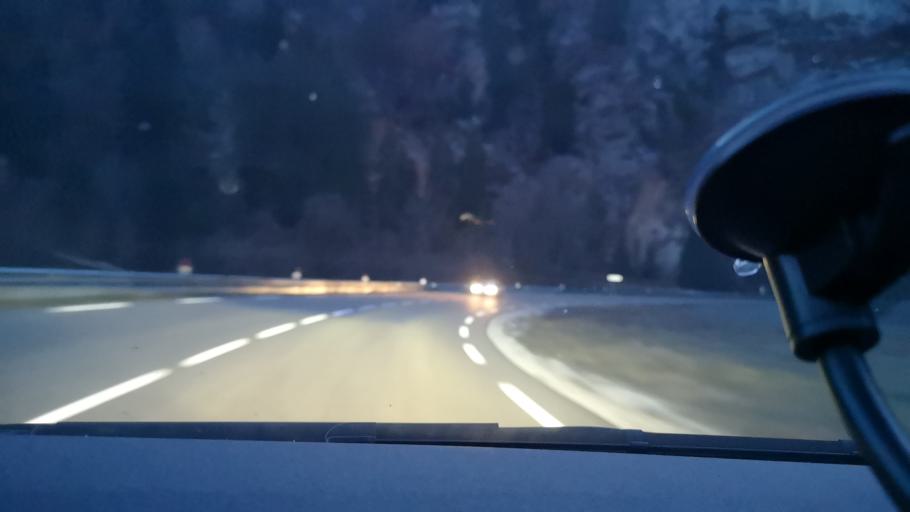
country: FR
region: Franche-Comte
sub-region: Departement du Jura
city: Champagnole
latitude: 46.7529
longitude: 5.9719
